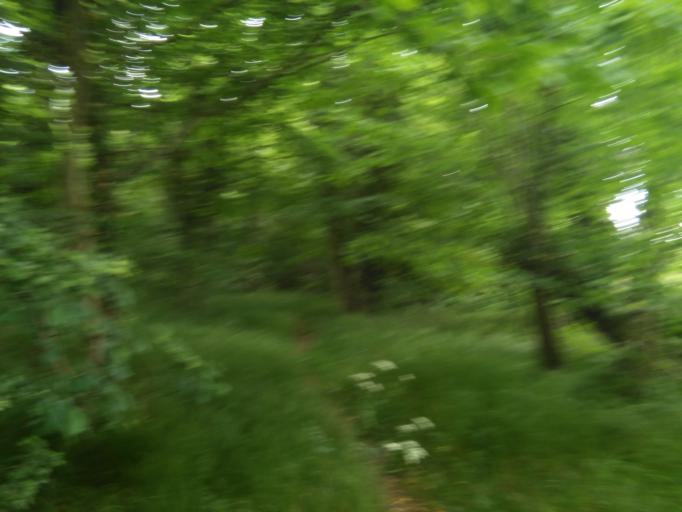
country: DK
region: Capital Region
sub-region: Bornholm Kommune
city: Akirkeby
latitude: 55.2370
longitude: 14.8709
